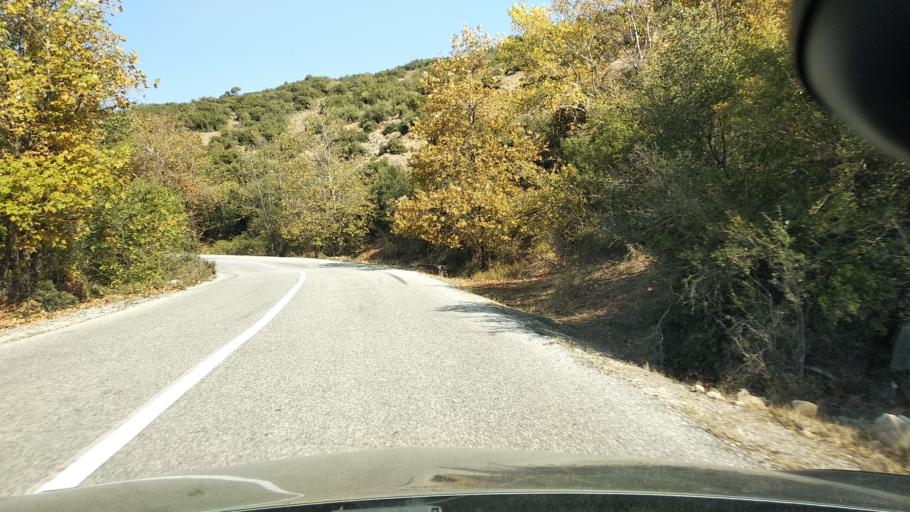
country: GR
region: Thessaly
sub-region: Trikala
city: Kalampaka
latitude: 39.7151
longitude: 21.6492
